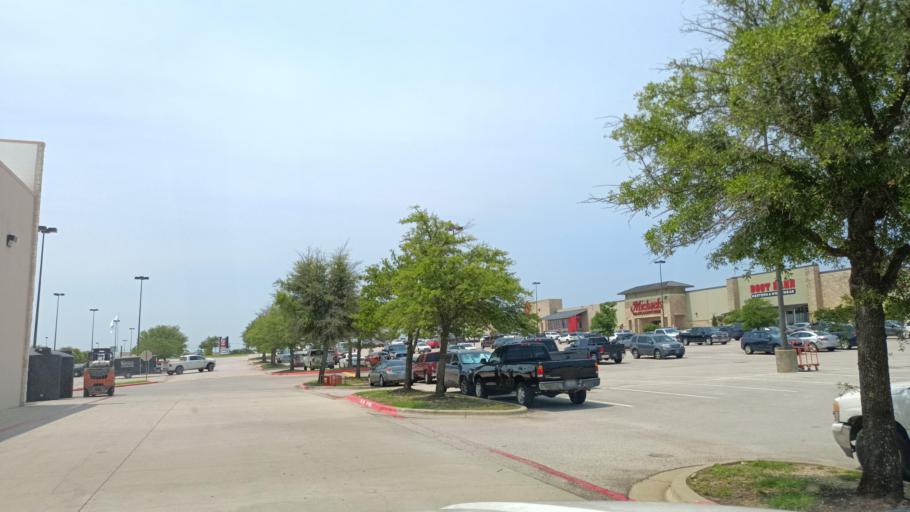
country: US
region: Texas
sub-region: Bell County
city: Temple
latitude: 31.0951
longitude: -97.3834
